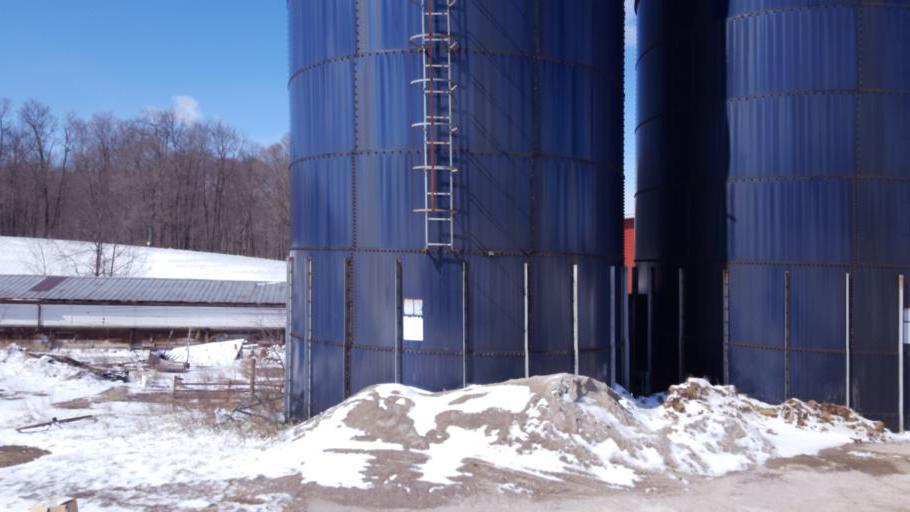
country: US
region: Ohio
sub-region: Knox County
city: Fredericktown
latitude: 40.5066
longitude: -82.6292
